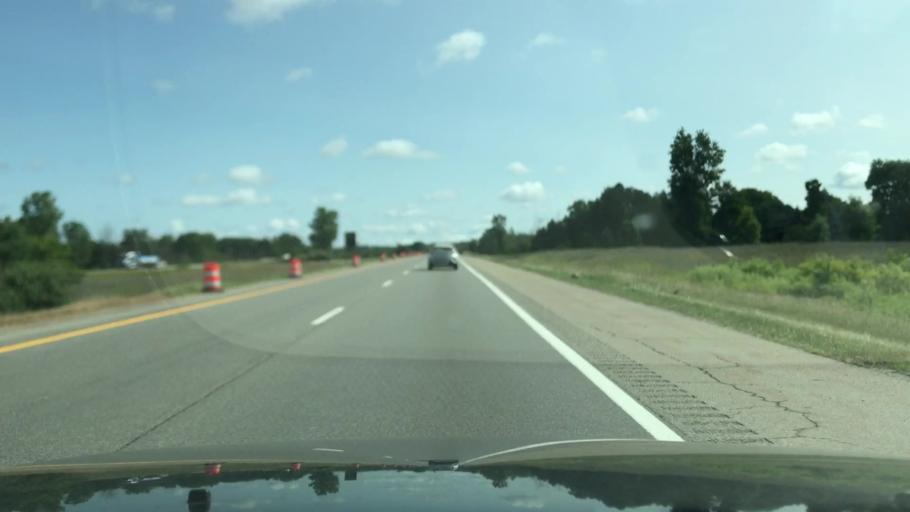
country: US
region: Michigan
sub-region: Kent County
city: Cedar Springs
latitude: 43.2542
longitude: -85.5552
